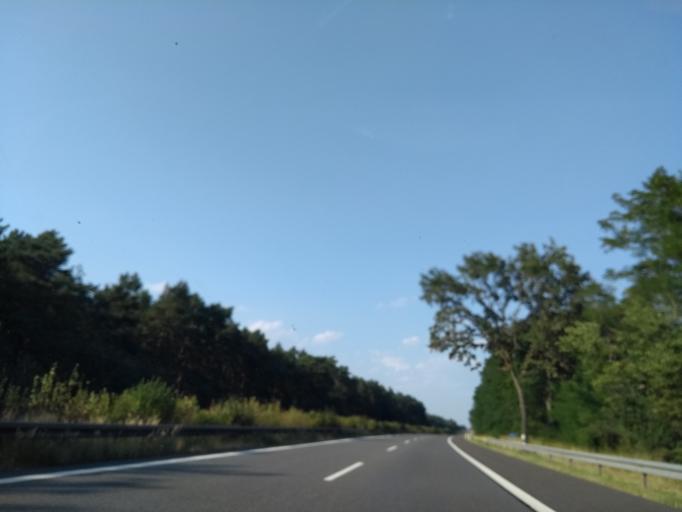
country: DE
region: Brandenburg
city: Lubbenau
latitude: 51.8104
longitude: 13.8885
